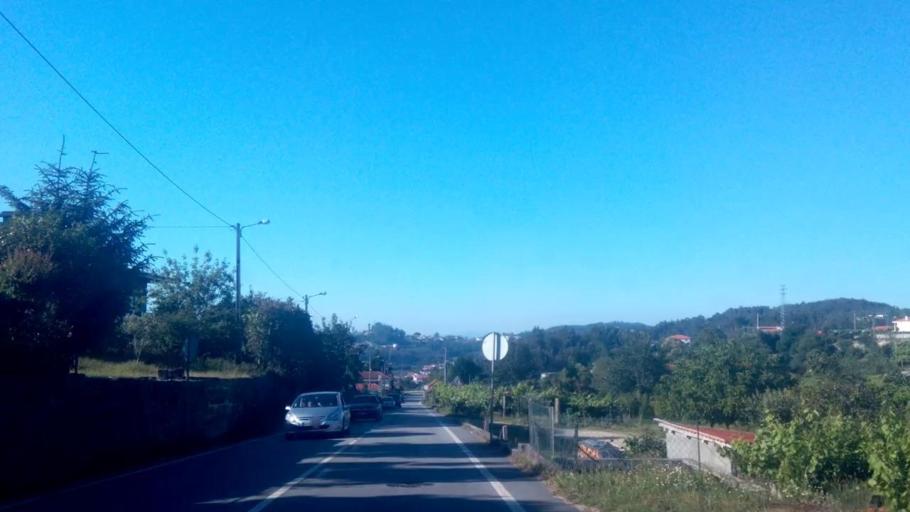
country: PT
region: Porto
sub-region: Penafiel
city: Penafiel
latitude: 41.1896
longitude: -8.2744
